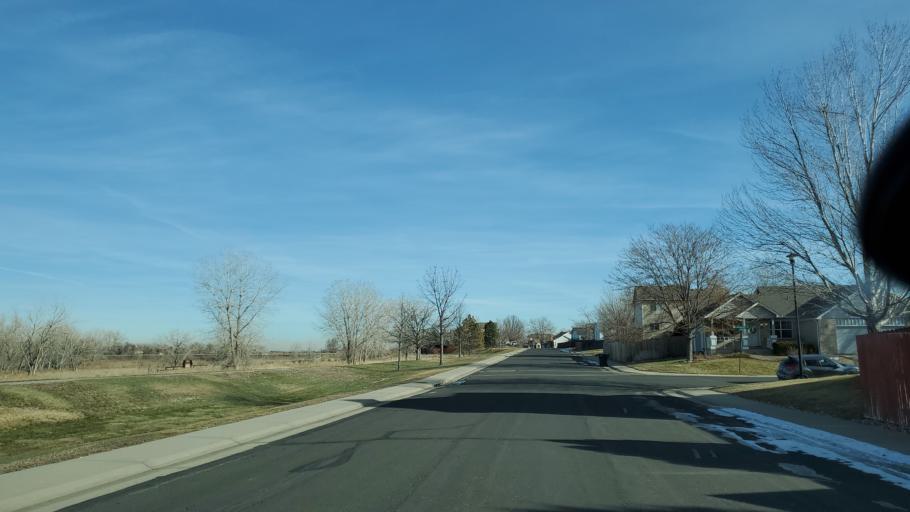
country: US
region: Colorado
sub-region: Adams County
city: Northglenn
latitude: 39.9169
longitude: -104.9575
